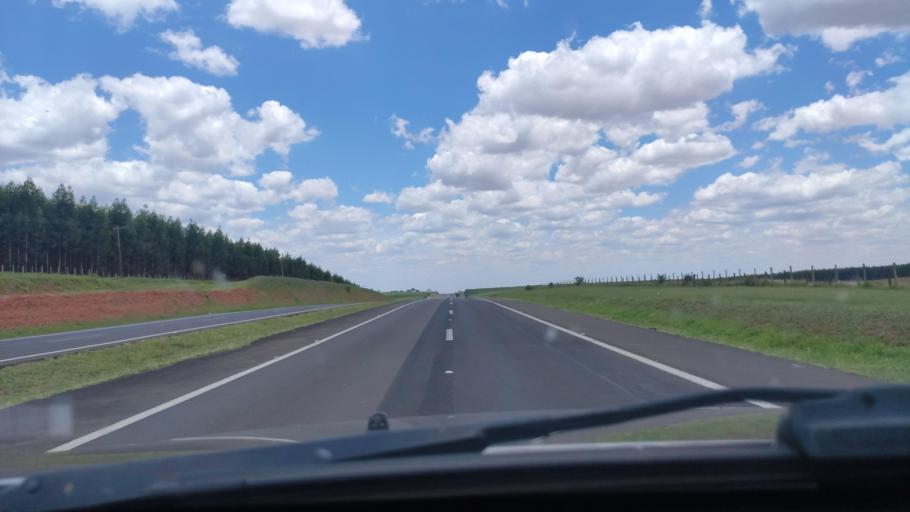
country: BR
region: Sao Paulo
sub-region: Duartina
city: Duartina
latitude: -22.6054
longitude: -49.3829
